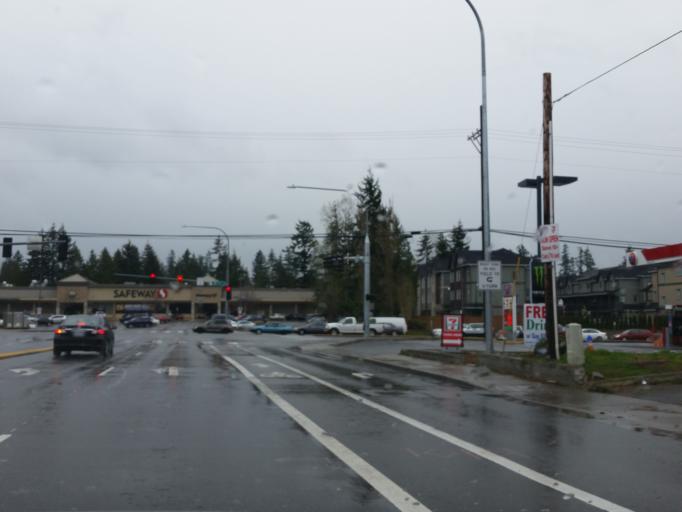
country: US
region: Washington
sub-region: Snohomish County
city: Mill Creek
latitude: 47.8971
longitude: -122.2077
